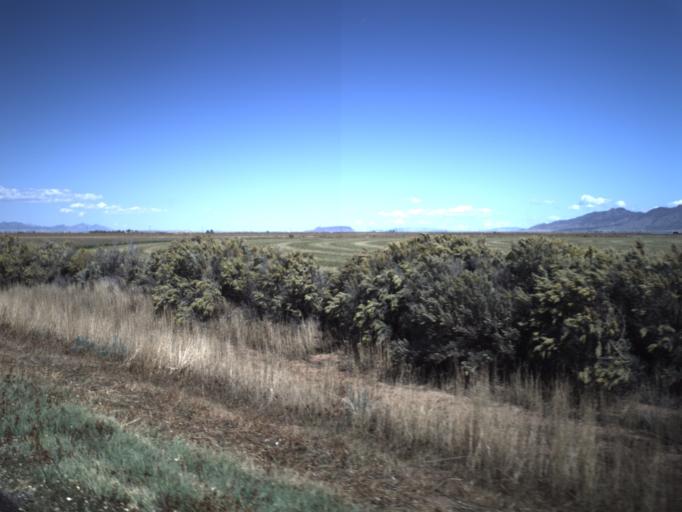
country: US
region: Utah
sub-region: Washington County
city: Enterprise
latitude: 37.6379
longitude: -113.6612
